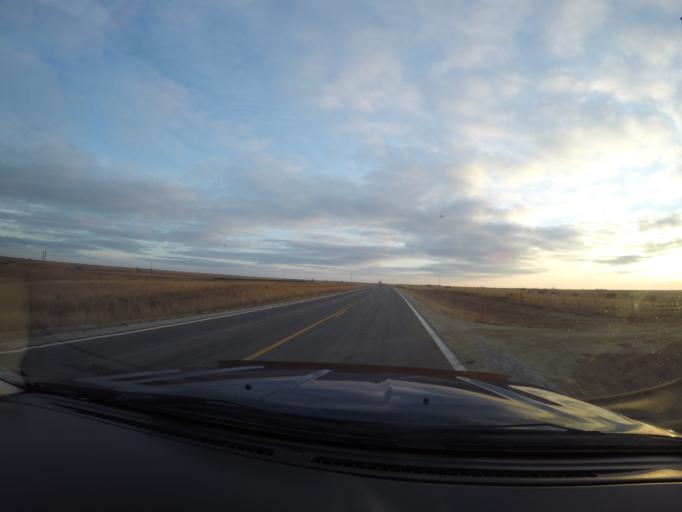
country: US
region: Kansas
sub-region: Morris County
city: Council Grove
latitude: 38.5653
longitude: -96.5219
